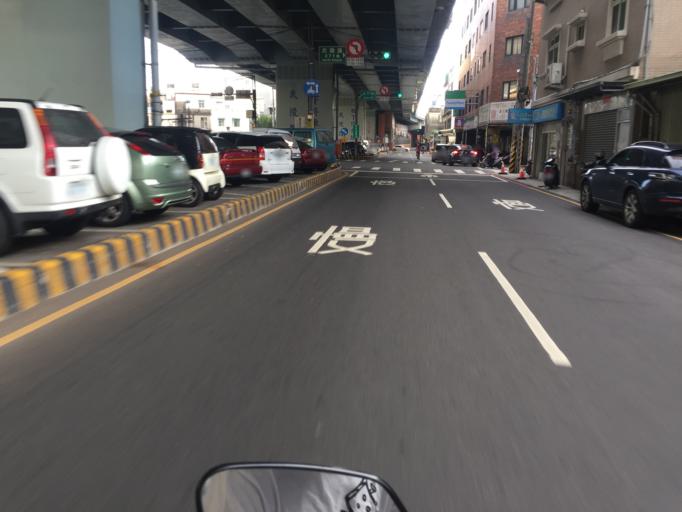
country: TW
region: Taiwan
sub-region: Hsinchu
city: Hsinchu
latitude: 24.8247
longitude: 120.9712
